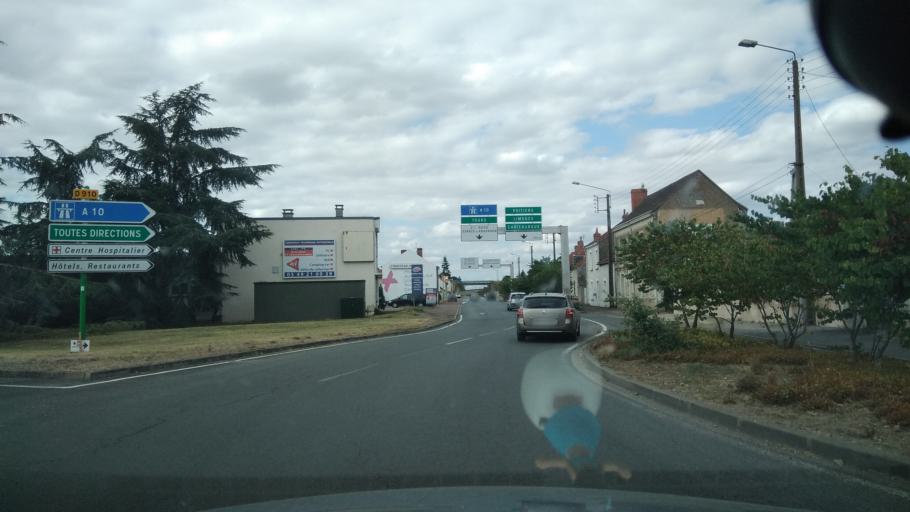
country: FR
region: Poitou-Charentes
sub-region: Departement de la Vienne
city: Antran
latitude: 46.8354
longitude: 0.5468
